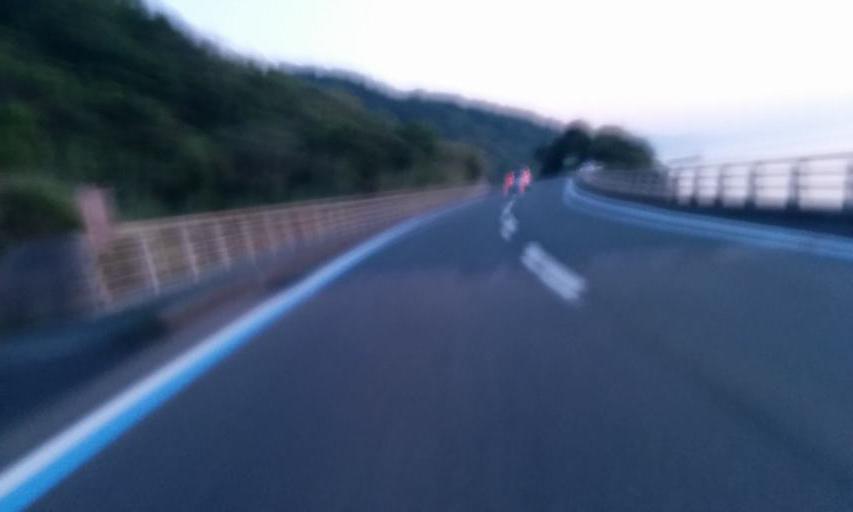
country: JP
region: Ehime
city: Ozu
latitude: 33.5815
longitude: 132.4477
